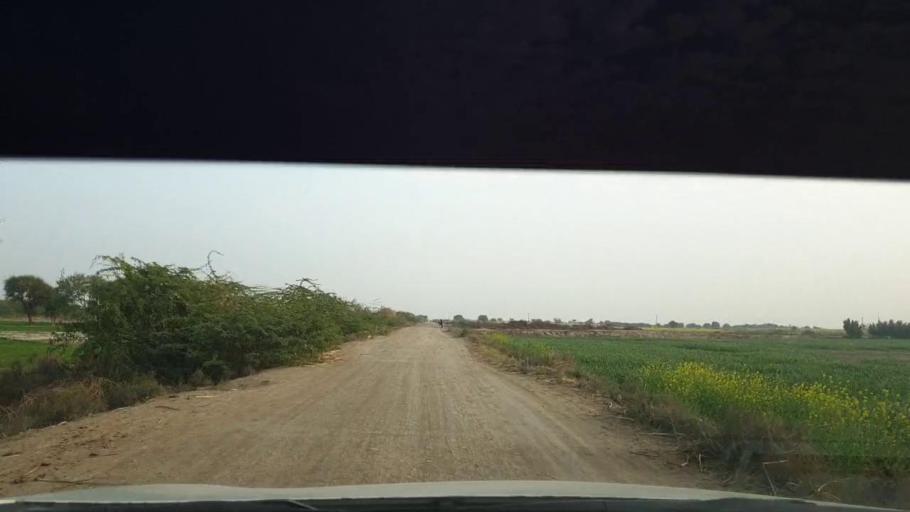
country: PK
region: Sindh
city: Berani
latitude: 25.7258
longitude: 68.9746
